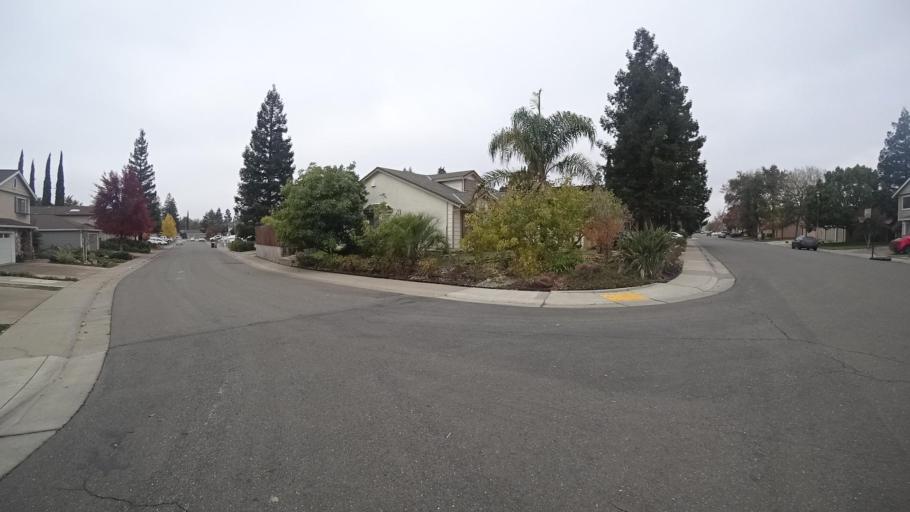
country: US
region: California
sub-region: Sacramento County
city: Elk Grove
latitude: 38.3986
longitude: -121.3619
